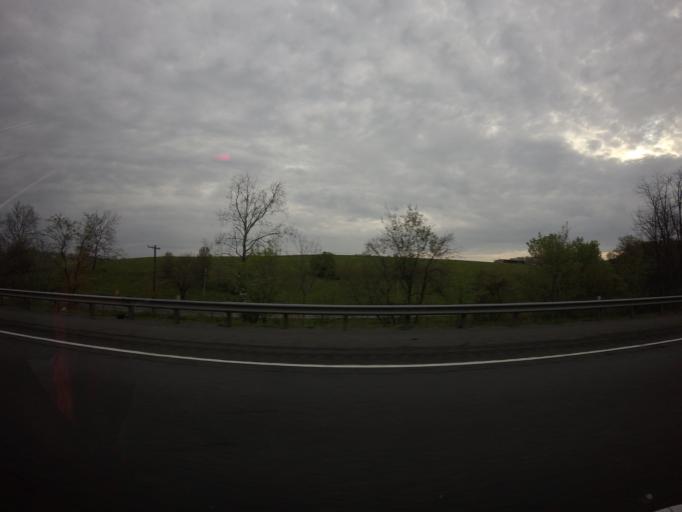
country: US
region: Maryland
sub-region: Carroll County
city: Mount Airy
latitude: 39.3628
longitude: -77.1788
